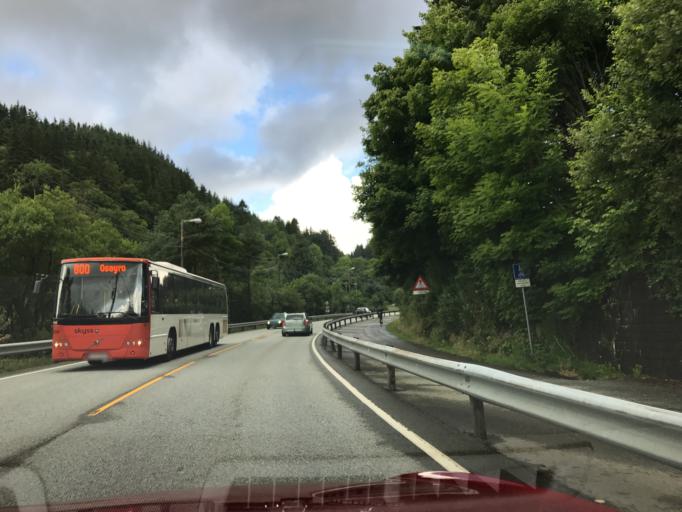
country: NO
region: Hordaland
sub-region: Os
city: Syfteland
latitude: 60.2902
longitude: 5.3831
